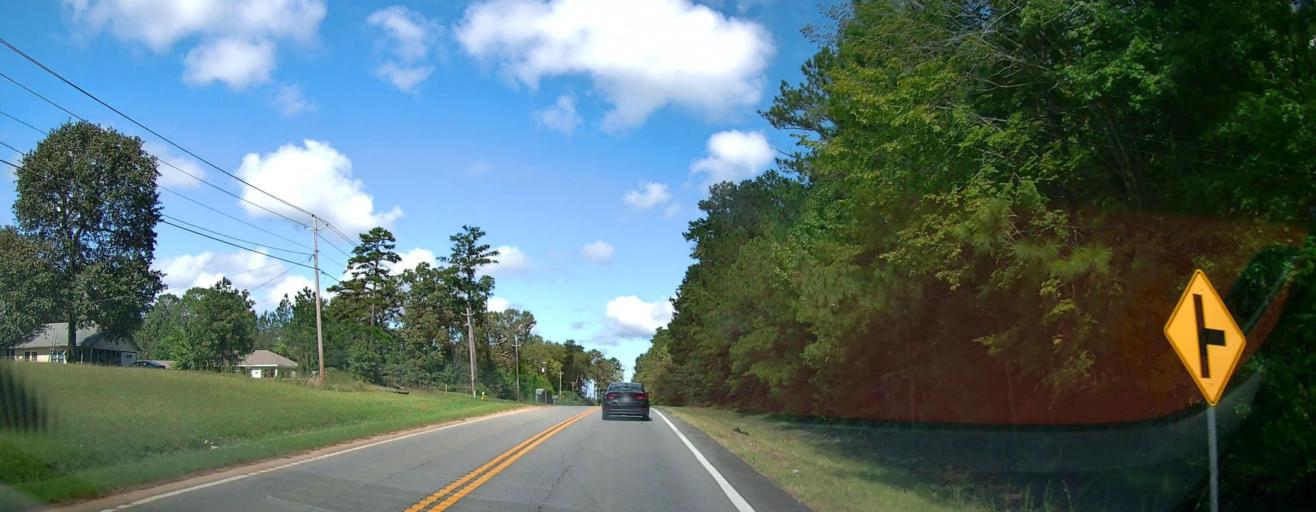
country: US
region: Georgia
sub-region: Bibb County
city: Macon
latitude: 32.8300
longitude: -83.5736
